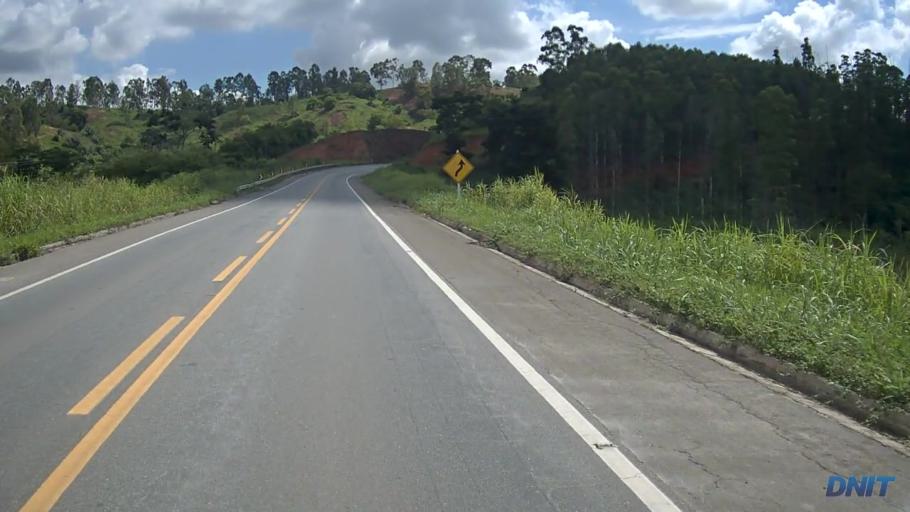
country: BR
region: Minas Gerais
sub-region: Belo Oriente
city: Belo Oriente
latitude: -19.0850
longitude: -42.1868
